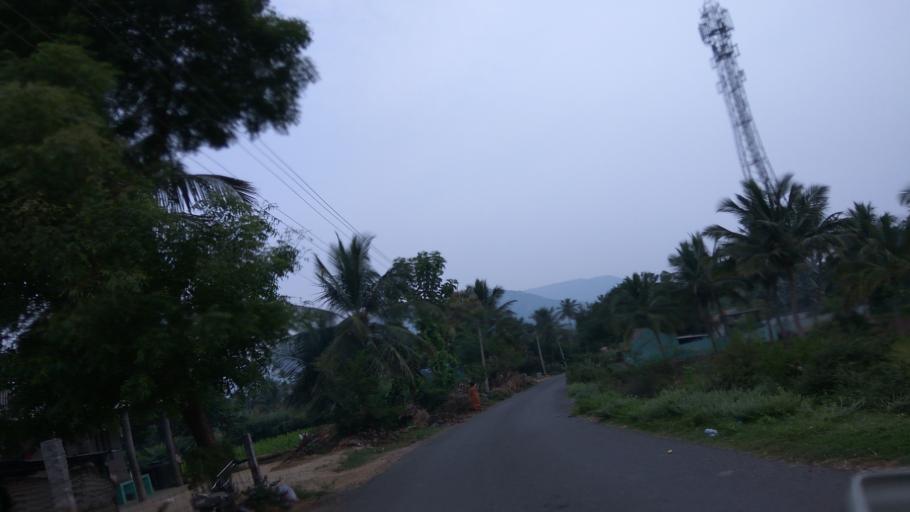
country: IN
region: Tamil Nadu
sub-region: Dharmapuri
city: Dharmapuri
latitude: 12.0217
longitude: 78.1158
